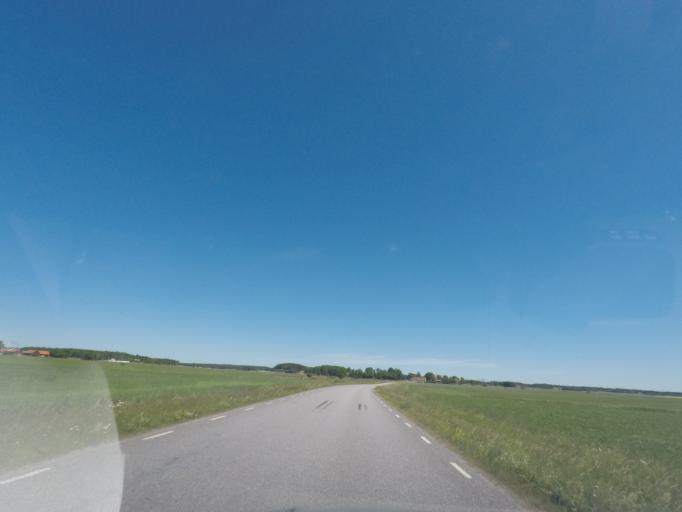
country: SE
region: Uppsala
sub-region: Enkopings Kommun
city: Irsta
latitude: 59.6900
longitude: 16.9650
